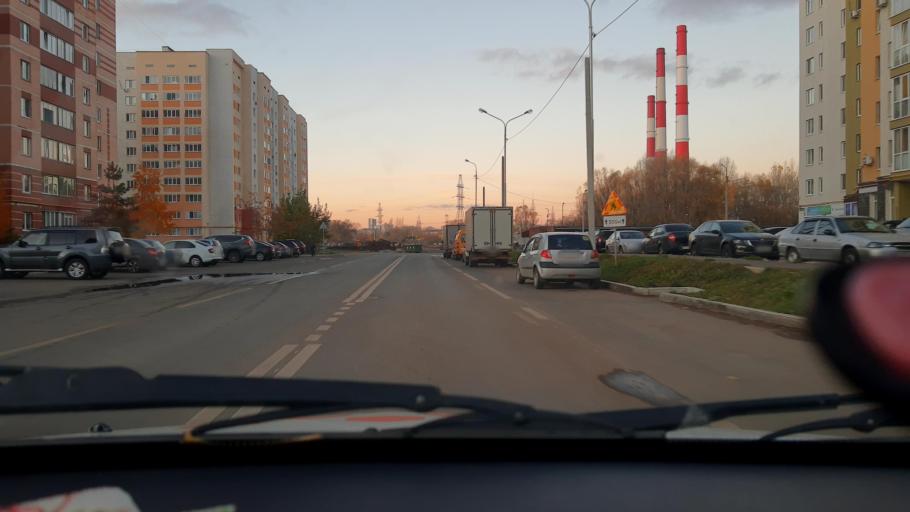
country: RU
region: Bashkortostan
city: Ufa
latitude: 54.7836
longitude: 56.1156
